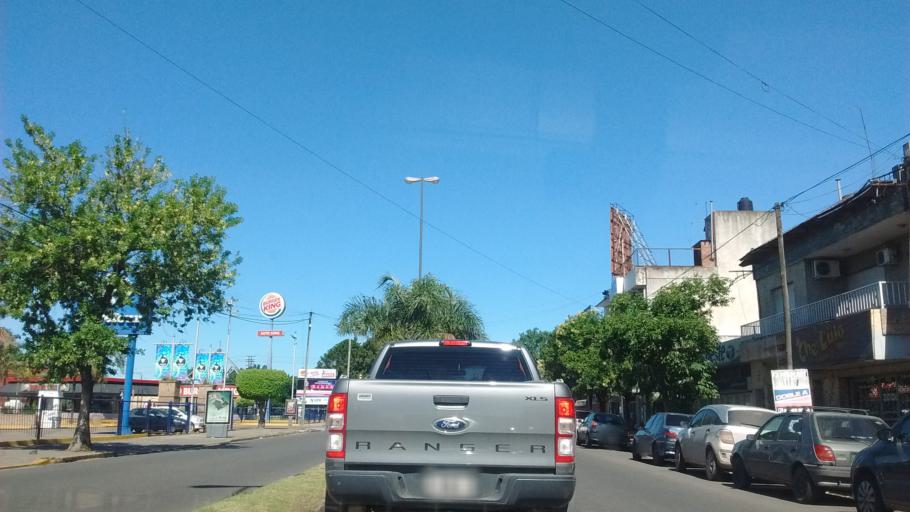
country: AR
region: Santa Fe
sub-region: Departamento de Rosario
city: Rosario
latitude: -32.9349
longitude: -60.7024
